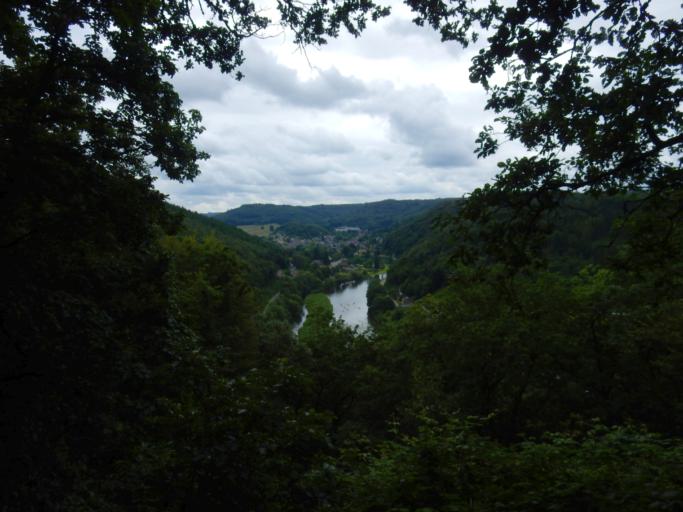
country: BE
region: Wallonia
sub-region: Province de Namur
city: Bievre
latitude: 49.8559
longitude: 4.9682
